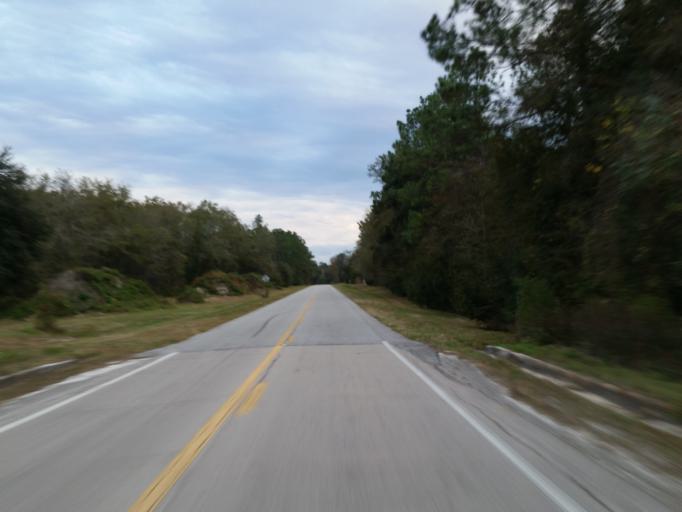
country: US
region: Georgia
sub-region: Echols County
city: Statenville
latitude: 30.5707
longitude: -83.0981
